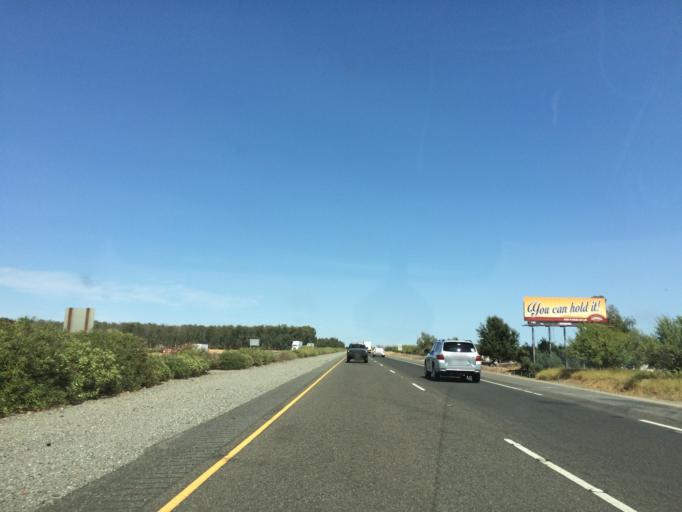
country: US
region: California
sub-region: Glenn County
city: Orland
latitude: 39.7571
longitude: -122.2053
